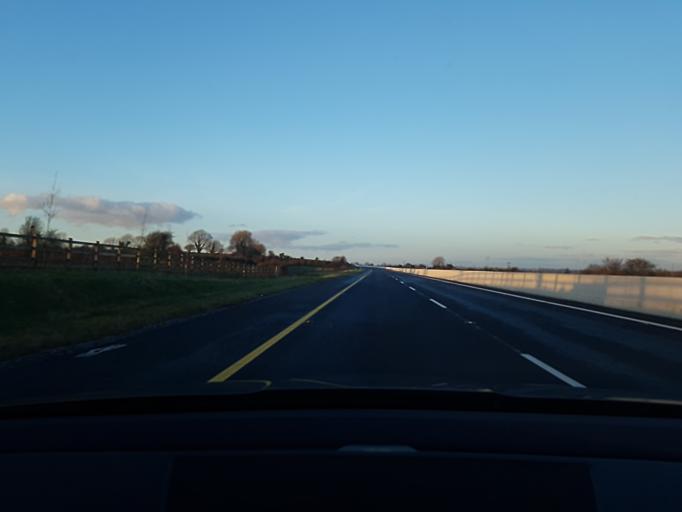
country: IE
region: Connaught
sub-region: County Galway
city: Tuam
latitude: 53.4810
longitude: -8.8635
